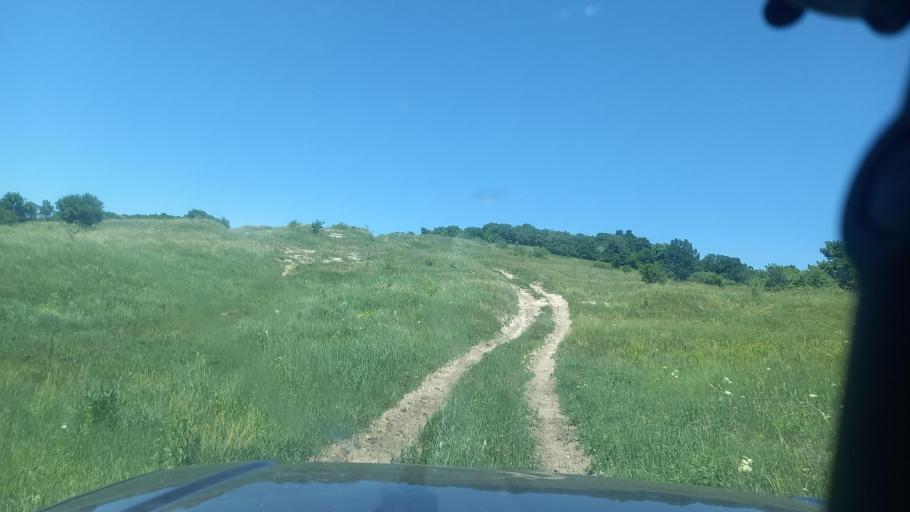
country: RU
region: Karachayevo-Cherkesiya
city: Pregradnaya
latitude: 44.1104
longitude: 41.1240
